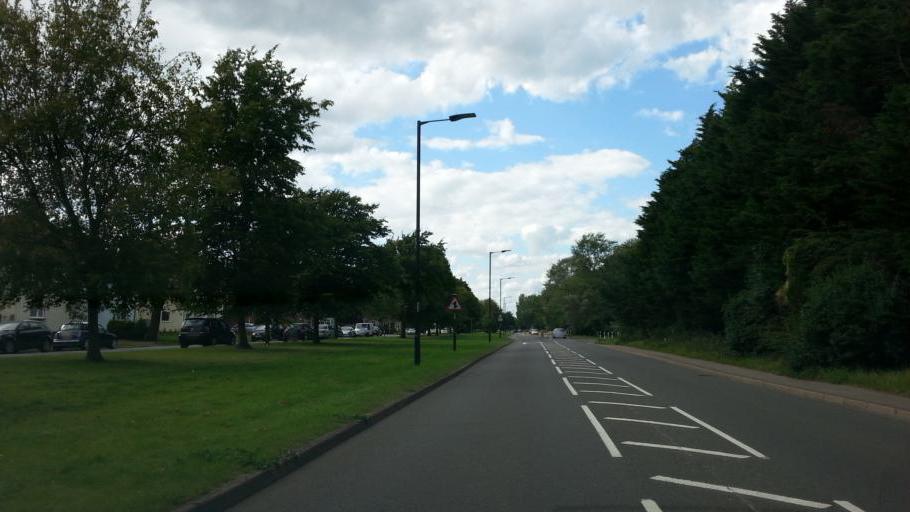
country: GB
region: England
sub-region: Suffolk
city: Bury St Edmunds
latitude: 52.2657
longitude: 0.7057
